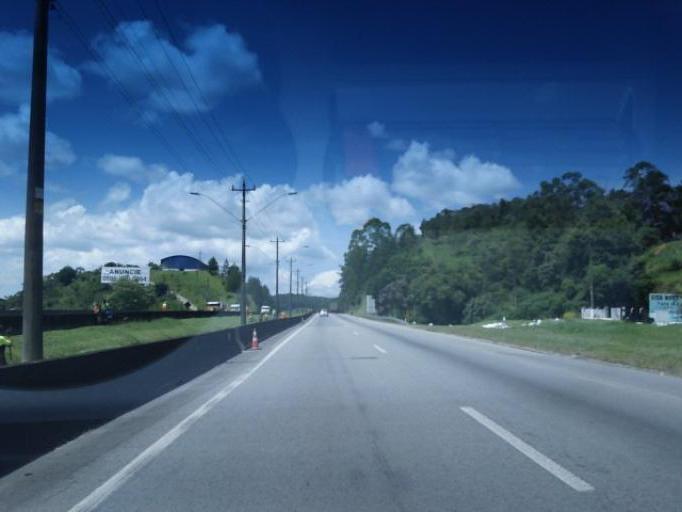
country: BR
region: Sao Paulo
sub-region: Sao Lourenco Da Serra
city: Sao Lourenco da Serra
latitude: -23.8982
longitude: -46.9875
